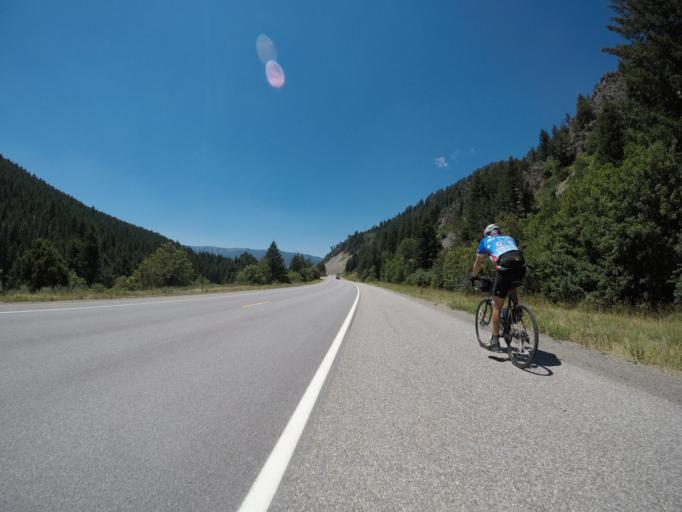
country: US
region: Wyoming
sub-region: Teton County
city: Hoback
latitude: 43.1777
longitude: -110.9914
